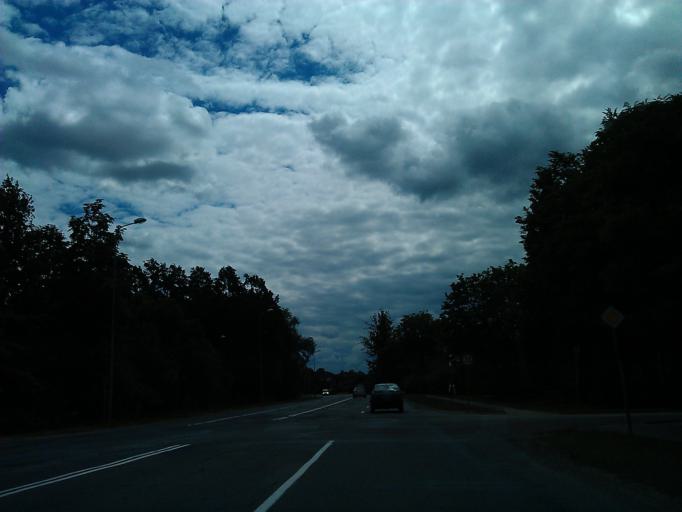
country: LV
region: Jelgava
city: Jelgava
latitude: 56.6464
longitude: 23.6924
